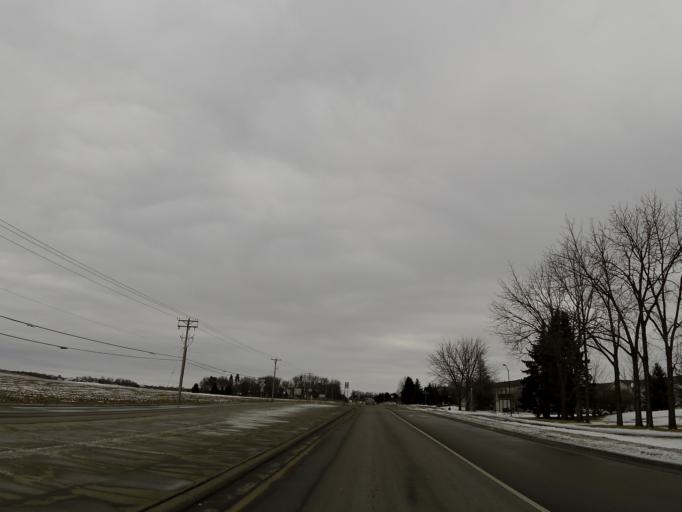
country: US
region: Minnesota
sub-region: Washington County
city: Cottage Grove
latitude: 44.8471
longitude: -92.9036
